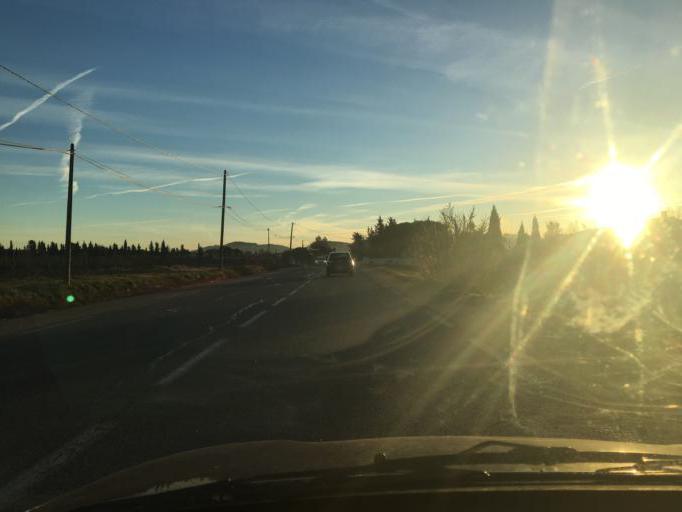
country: FR
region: Provence-Alpes-Cote d'Azur
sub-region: Departement du Var
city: Les Arcs
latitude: 43.4495
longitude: 6.4699
